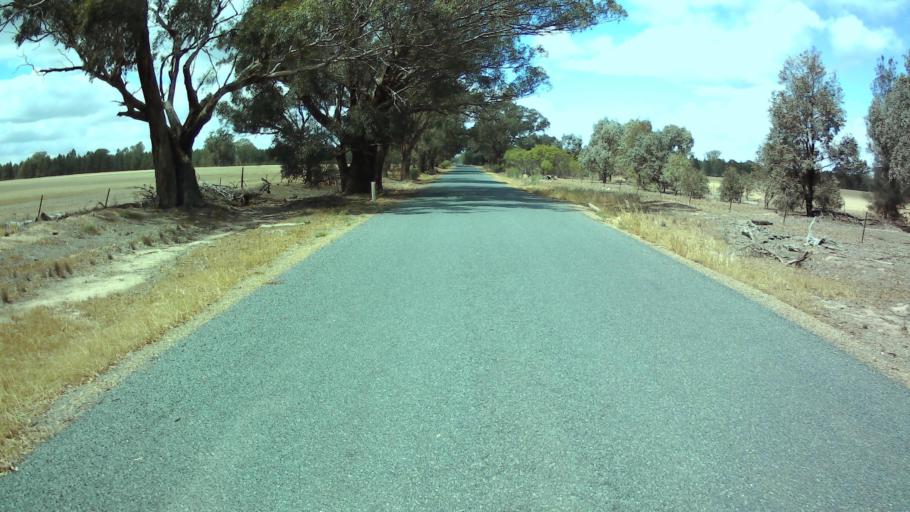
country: AU
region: New South Wales
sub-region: Weddin
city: Grenfell
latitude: -33.8946
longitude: 147.9219
